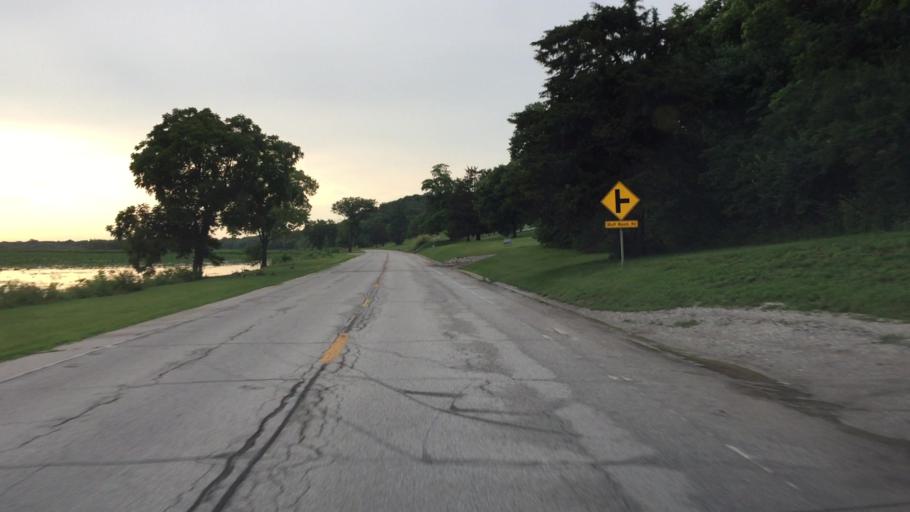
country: US
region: Illinois
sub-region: Hancock County
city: Nauvoo
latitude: 40.5252
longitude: -91.3679
